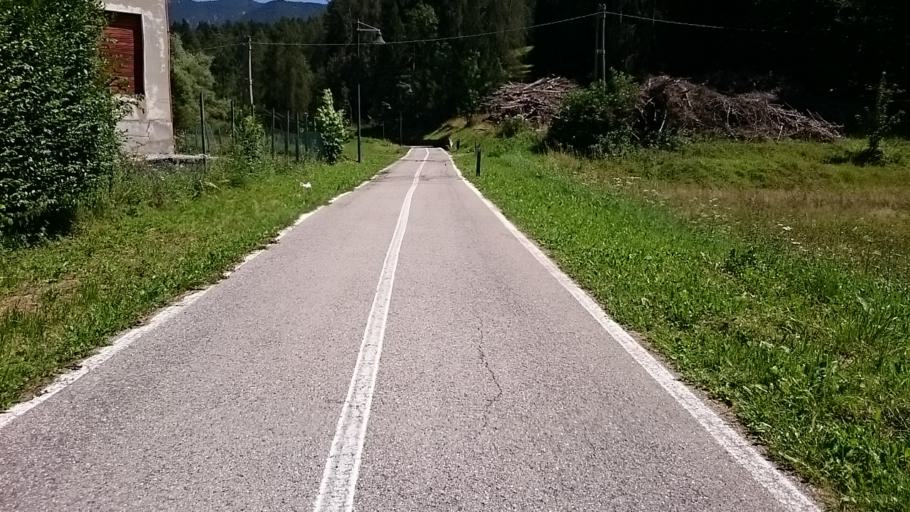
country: IT
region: Veneto
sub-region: Provincia di Belluno
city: Pieve di Cadore
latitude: 46.4197
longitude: 12.3514
